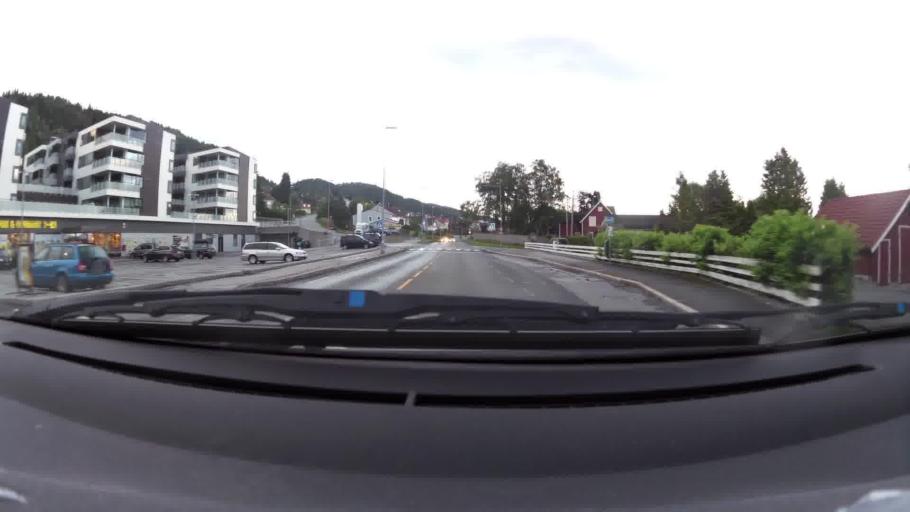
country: NO
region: More og Romsdal
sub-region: Molde
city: Molde
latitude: 62.7441
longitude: 7.1984
